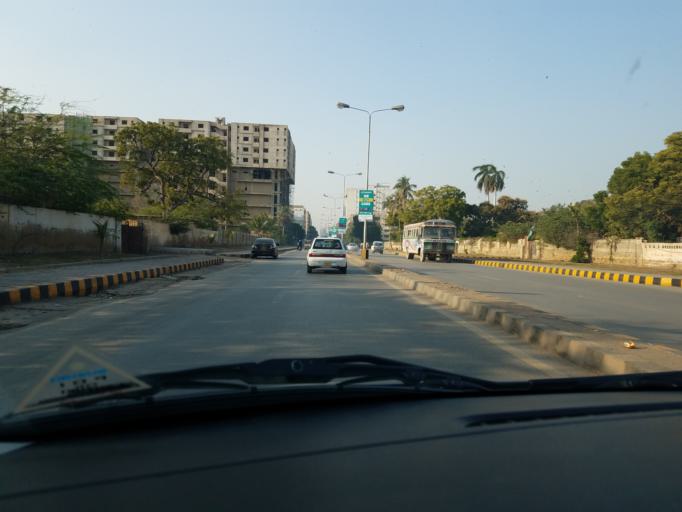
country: PK
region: Sindh
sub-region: Karachi District
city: Karachi
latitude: 24.8545
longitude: 67.0331
